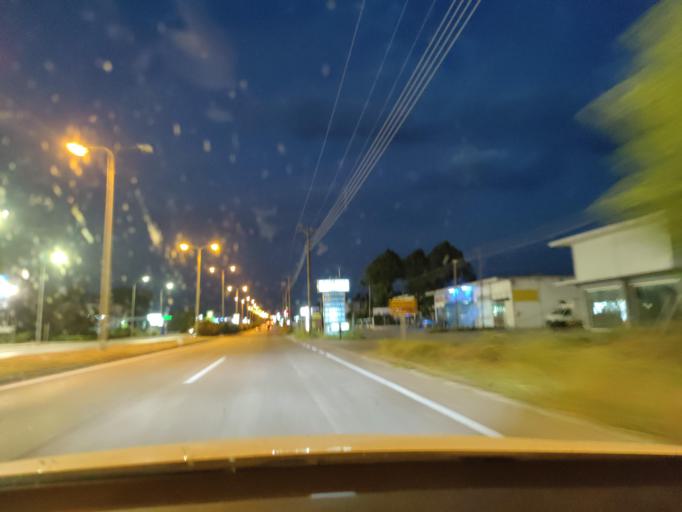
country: GR
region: Central Macedonia
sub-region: Nomos Serron
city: Lefkonas
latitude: 41.0912
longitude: 23.5143
